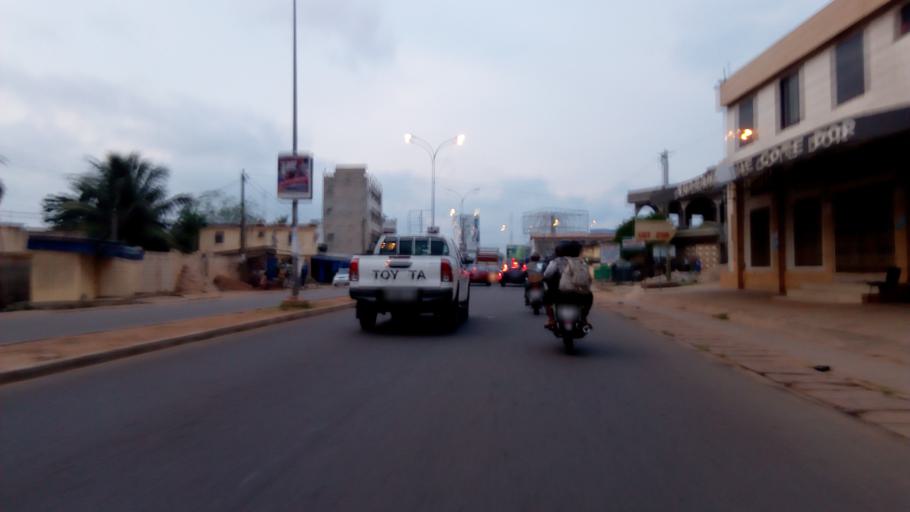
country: TG
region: Maritime
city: Lome
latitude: 6.2021
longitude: 1.1826
